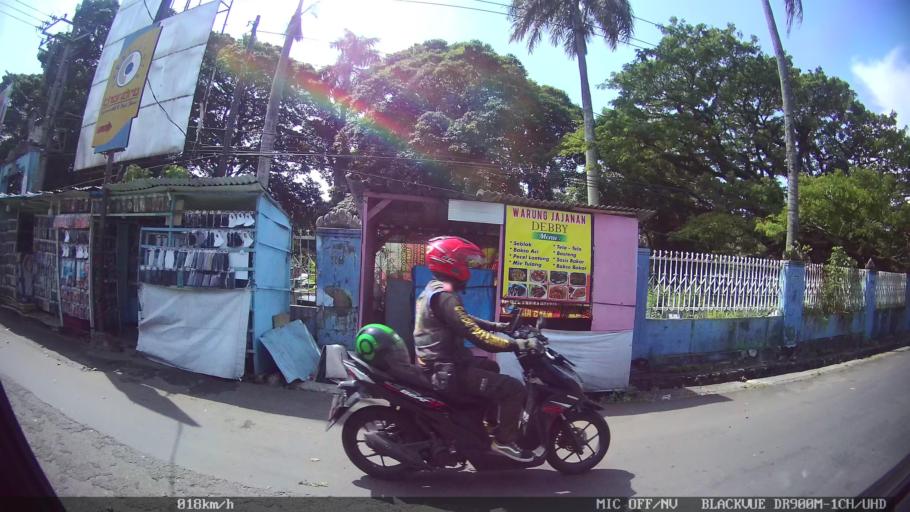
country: ID
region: Lampung
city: Bandarlampung
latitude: -5.4142
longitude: 105.2617
